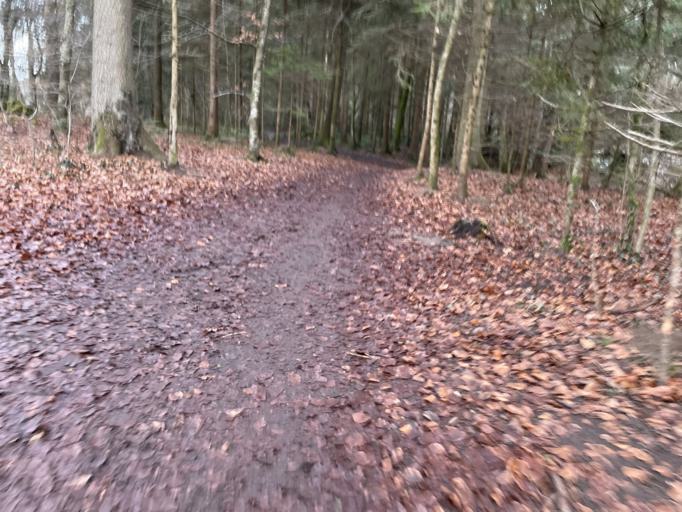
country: CH
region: Bern
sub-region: Thun District
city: Uttigen
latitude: 46.8098
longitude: 7.5694
